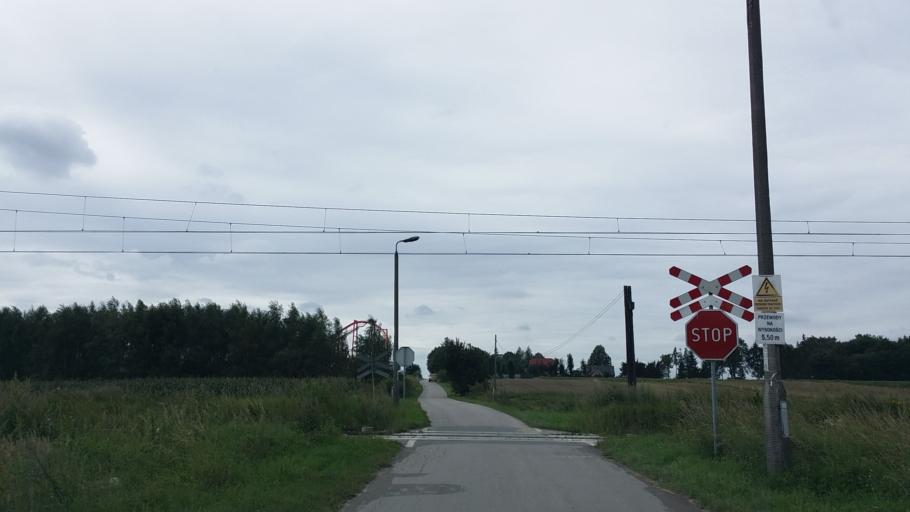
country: PL
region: Lesser Poland Voivodeship
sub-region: Powiat oswiecimski
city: Przeciszow
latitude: 50.0057
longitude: 19.4048
